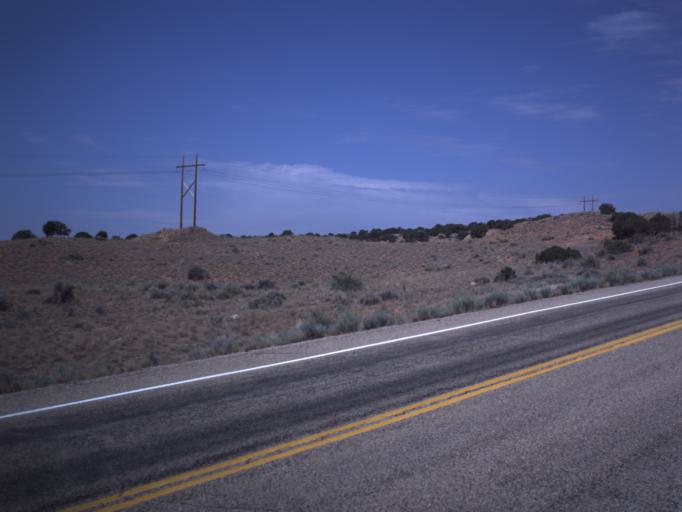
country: US
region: Utah
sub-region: Uintah County
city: Naples
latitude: 40.1376
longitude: -109.2702
